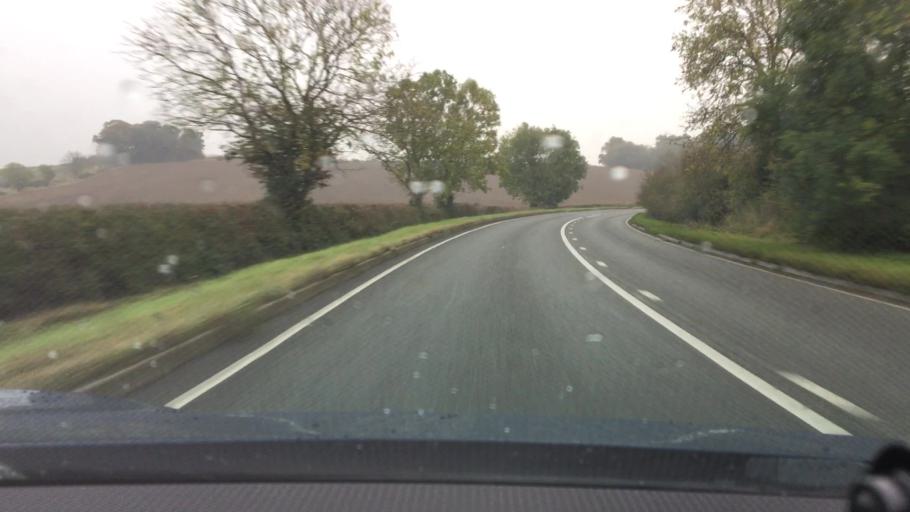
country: GB
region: England
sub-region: Leicestershire
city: Market Harborough
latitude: 52.4787
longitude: -0.9508
